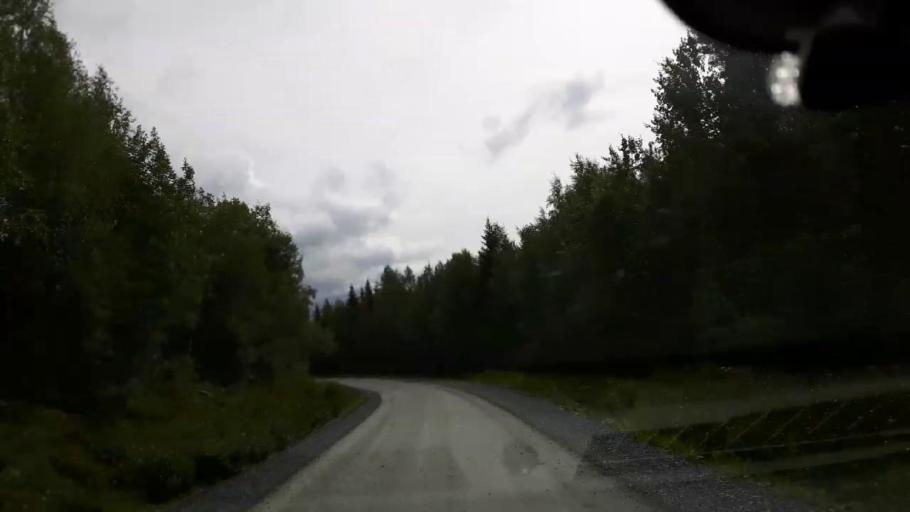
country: SE
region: Jaemtland
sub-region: Krokoms Kommun
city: Valla
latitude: 63.5912
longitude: 14.1434
